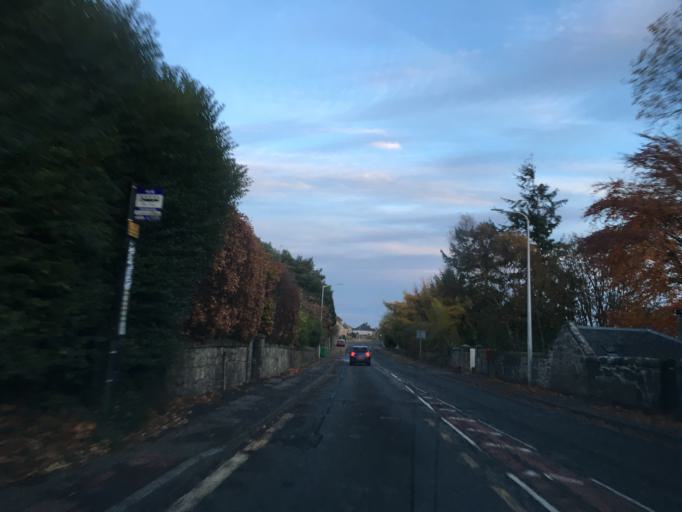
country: GB
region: Scotland
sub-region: Fife
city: Crossford
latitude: 56.0819
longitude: -3.4992
